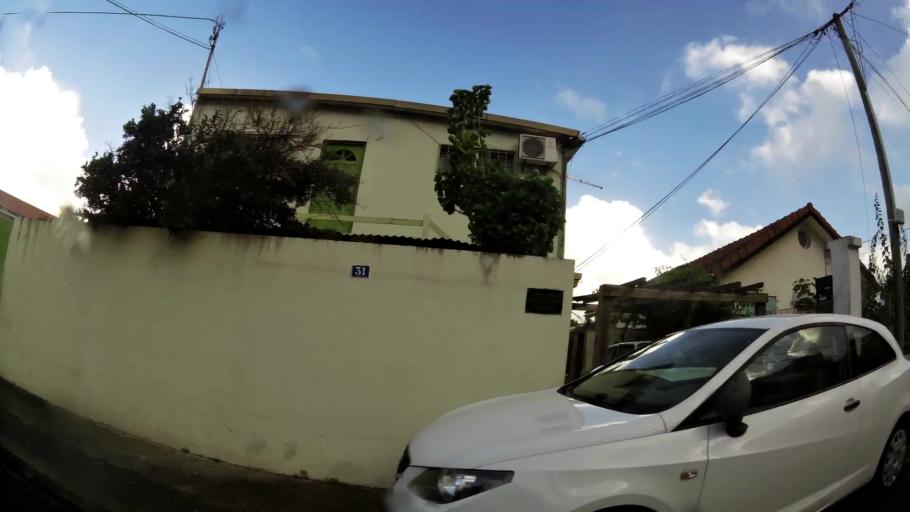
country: MQ
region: Martinique
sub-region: Martinique
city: Fort-de-France
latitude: 14.6069
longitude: -61.0751
